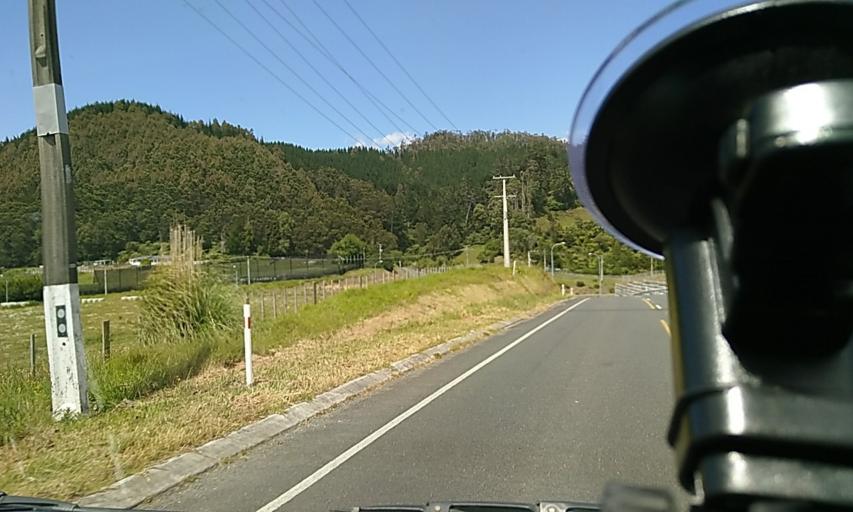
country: NZ
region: Bay of Plenty
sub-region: Western Bay of Plenty District
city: Waihi Beach
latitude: -37.4583
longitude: 175.9316
